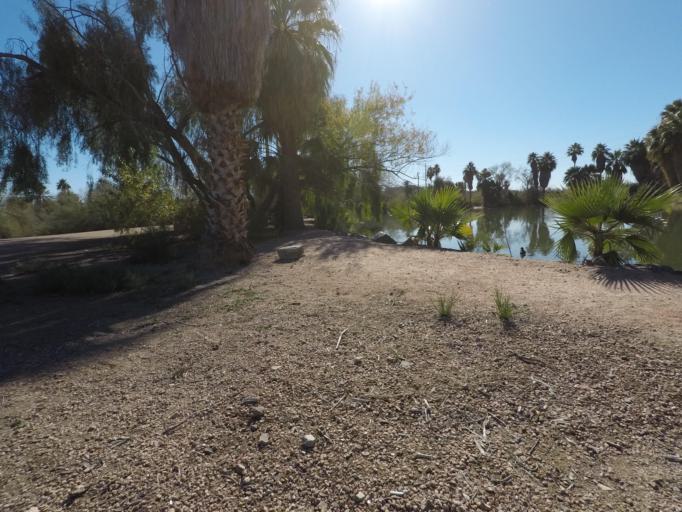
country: US
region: Arizona
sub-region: Maricopa County
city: Tempe Junction
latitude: 33.4502
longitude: -111.9378
